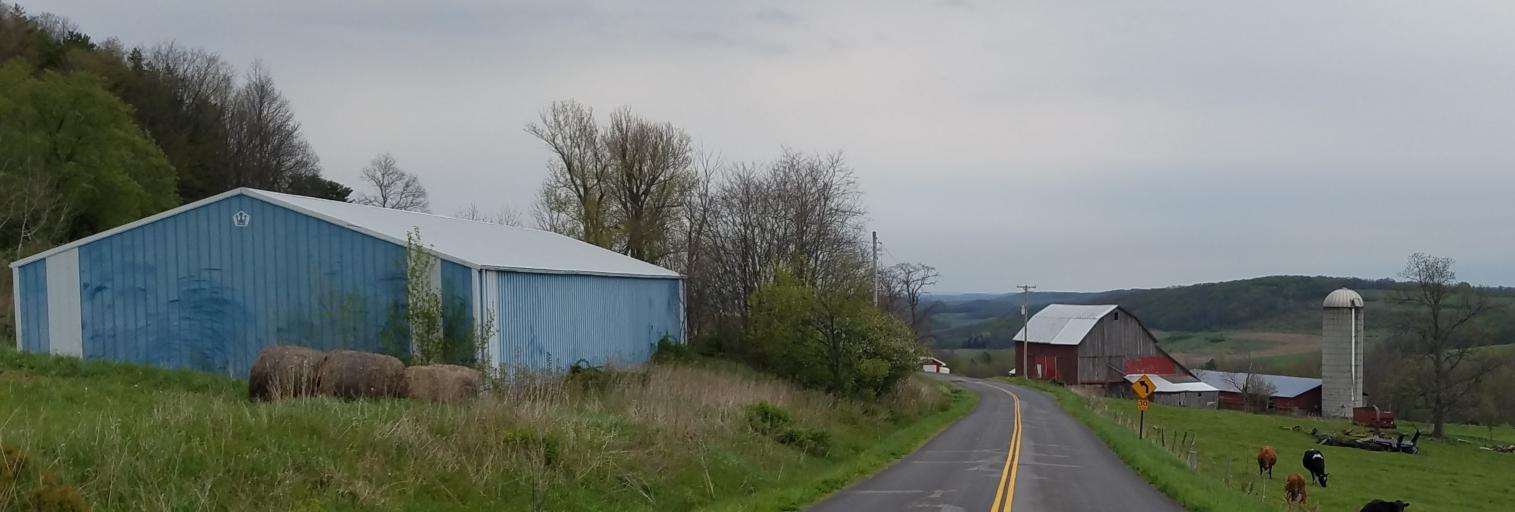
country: US
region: New York
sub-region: Steuben County
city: Canisteo
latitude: 42.1460
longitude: -77.5611
